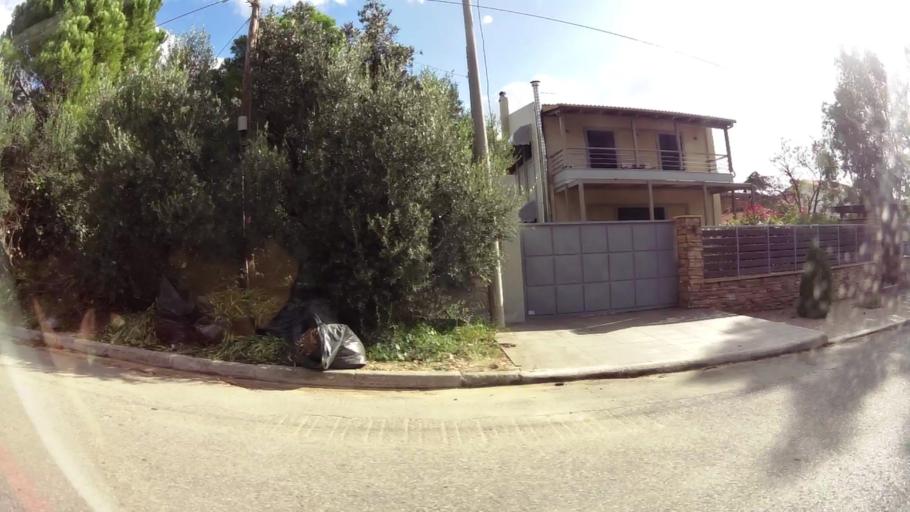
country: GR
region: Attica
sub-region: Nomarchia Anatolikis Attikis
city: Thrakomakedones
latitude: 38.1312
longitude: 23.7641
